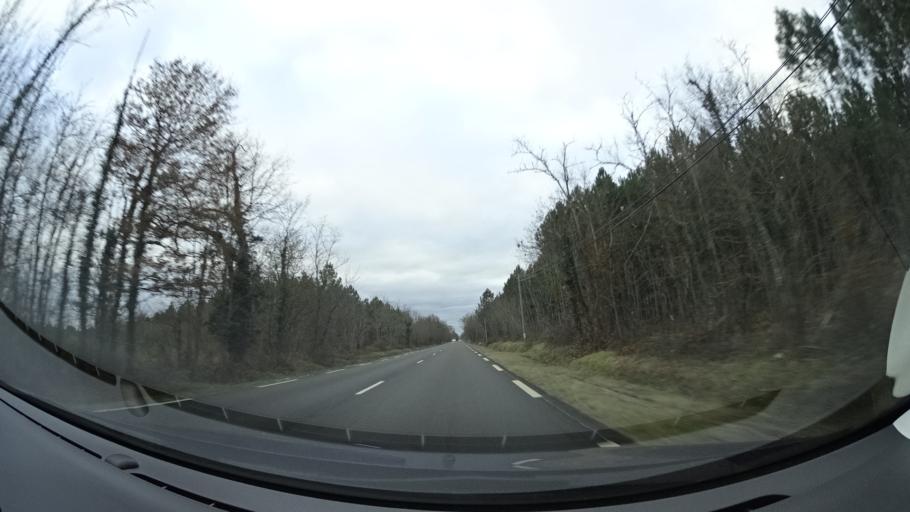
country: FR
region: Aquitaine
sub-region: Departement des Landes
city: Sarbazan
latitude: 43.9541
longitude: -0.3511
